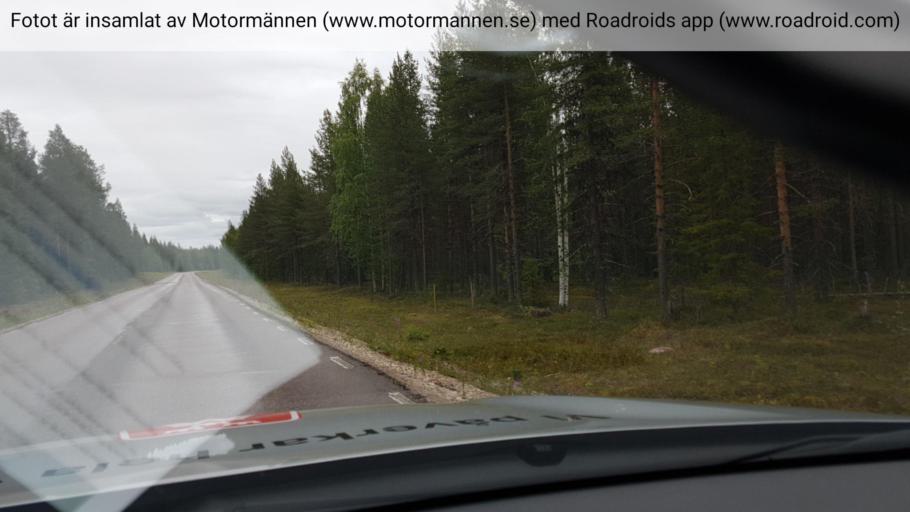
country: SE
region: Norrbotten
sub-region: Overkalix Kommun
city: OEverkalix
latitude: 67.0619
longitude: 22.2814
